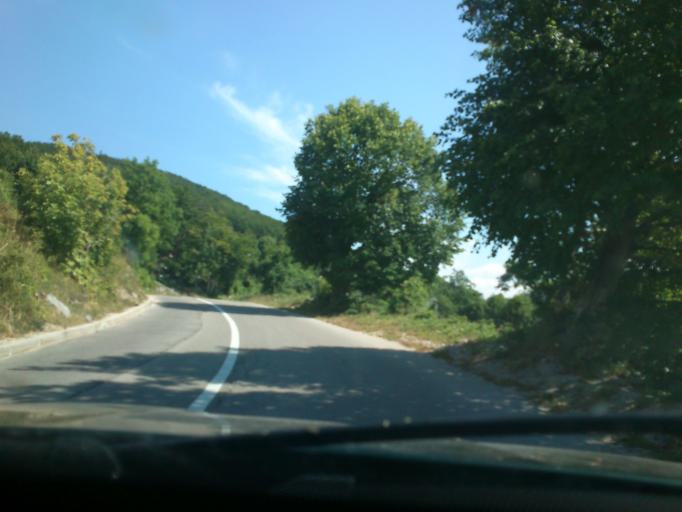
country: HR
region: Licko-Senjska
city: Senj
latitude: 44.8711
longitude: 14.9850
